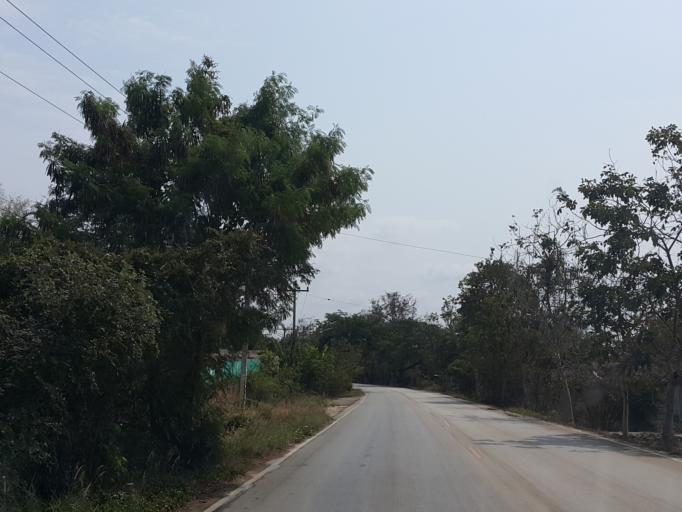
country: TH
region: Lamphun
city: Ban Thi
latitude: 18.6646
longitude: 99.0991
